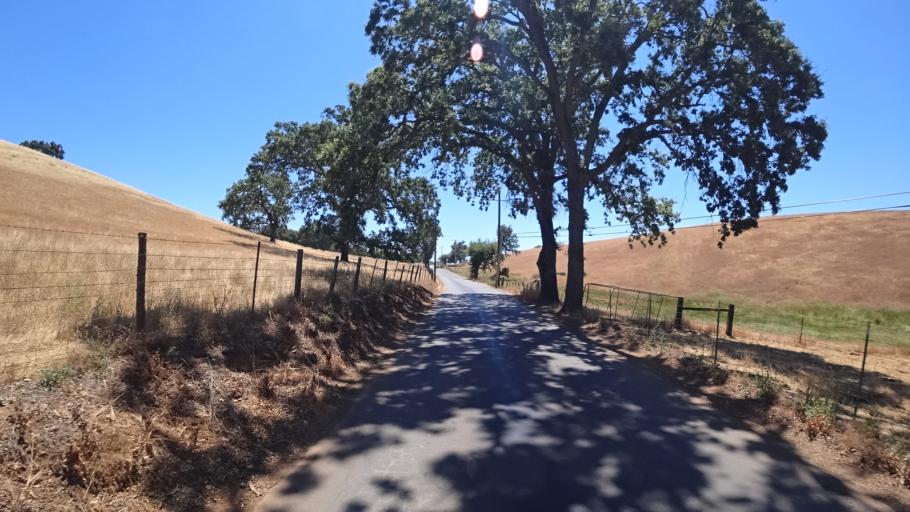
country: US
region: California
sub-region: Calaveras County
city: Mountain Ranch
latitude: 38.2357
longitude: -120.5547
